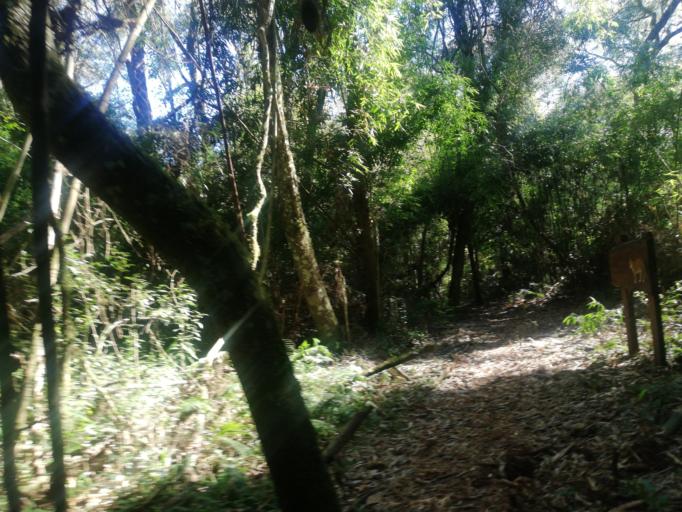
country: AR
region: Misiones
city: Colonia Wanda
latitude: -25.8574
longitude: -54.1667
